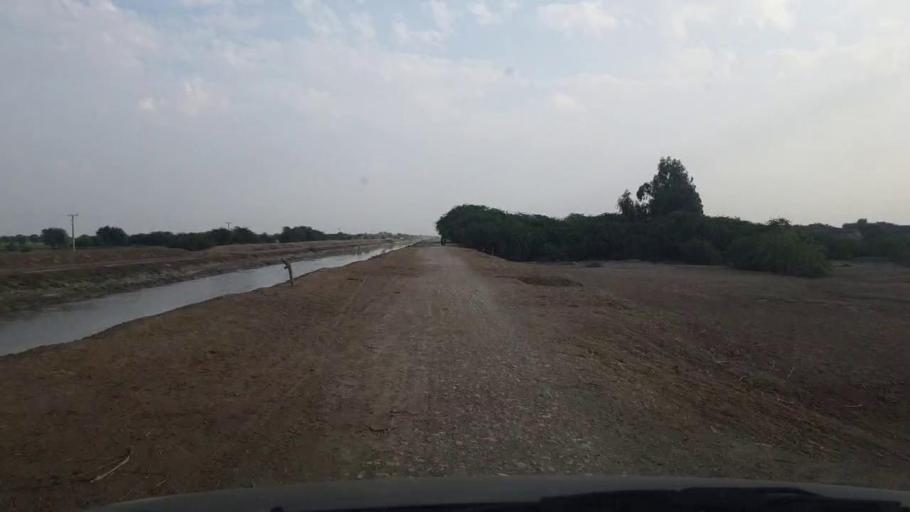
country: PK
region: Sindh
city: Badin
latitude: 24.5252
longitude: 68.6805
